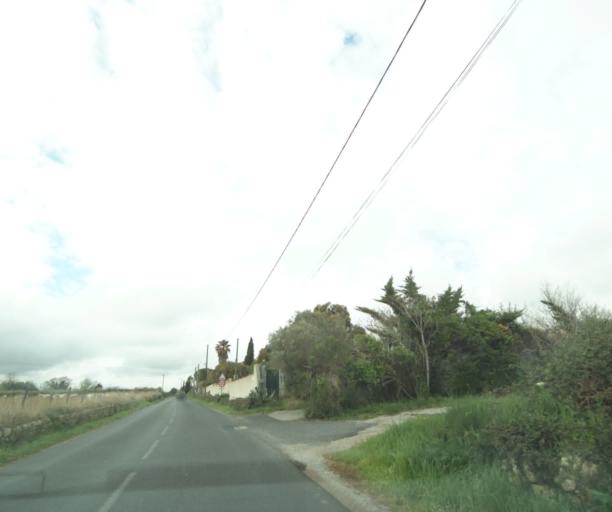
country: FR
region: Languedoc-Roussillon
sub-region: Departement de l'Herault
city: Saussan
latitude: 43.5646
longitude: 3.7754
